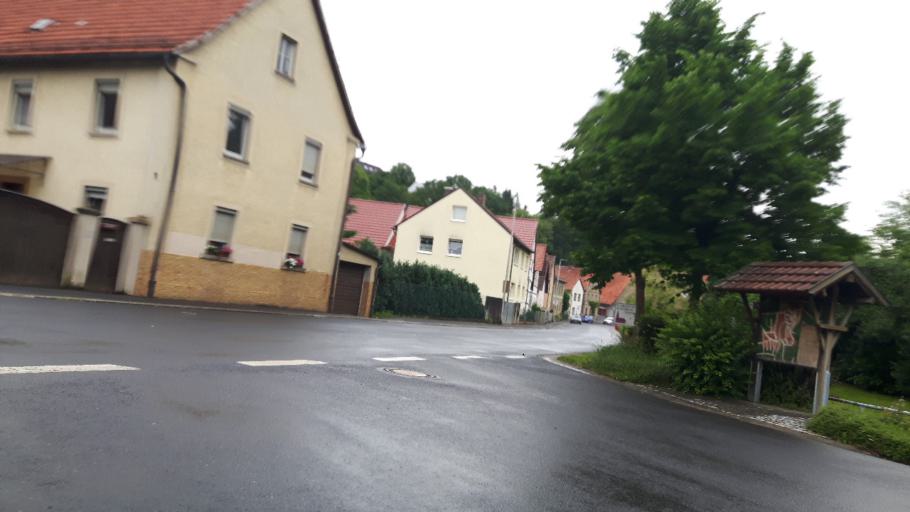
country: DE
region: Bavaria
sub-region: Regierungsbezirk Unterfranken
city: Uchtelhausen
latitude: 50.0925
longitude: 10.2484
